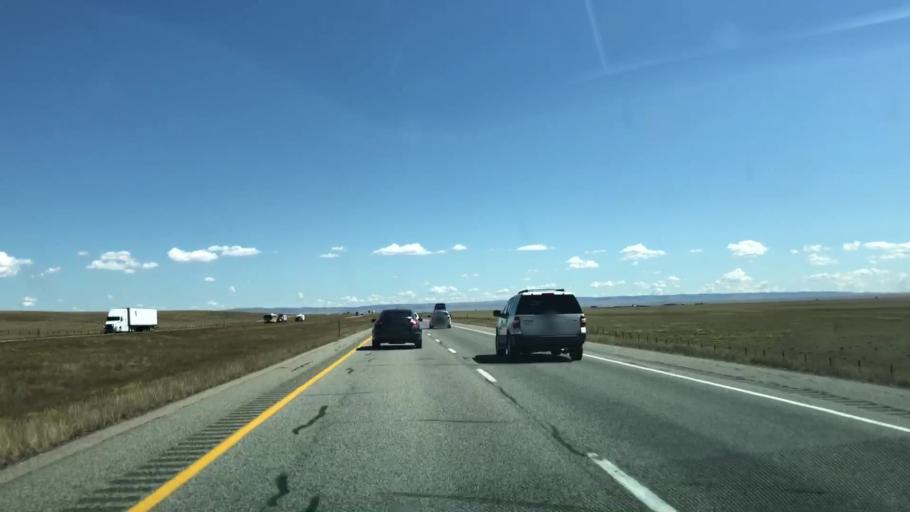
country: US
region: Wyoming
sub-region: Albany County
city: Laramie
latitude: 41.4368
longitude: -105.9191
